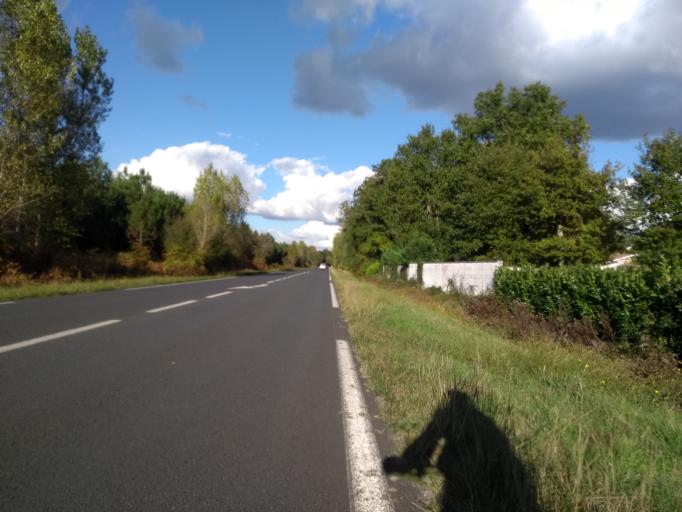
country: FR
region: Aquitaine
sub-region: Departement de la Gironde
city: Cestas
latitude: 44.7179
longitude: -0.6895
